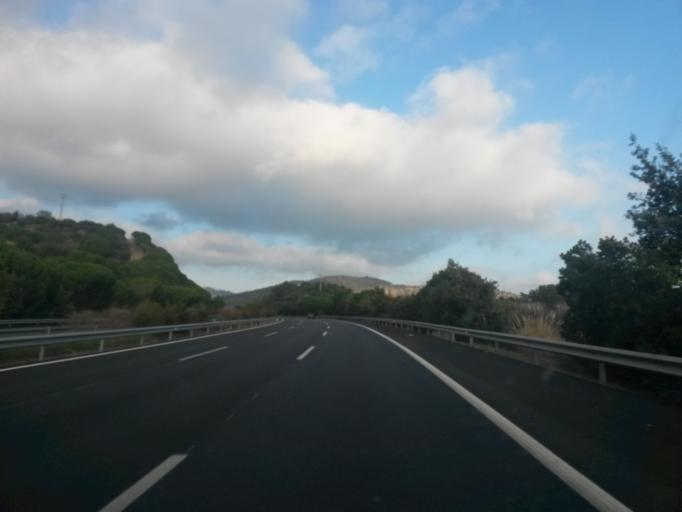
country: ES
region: Catalonia
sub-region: Provincia de Barcelona
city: Calella
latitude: 41.6324
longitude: 2.6691
